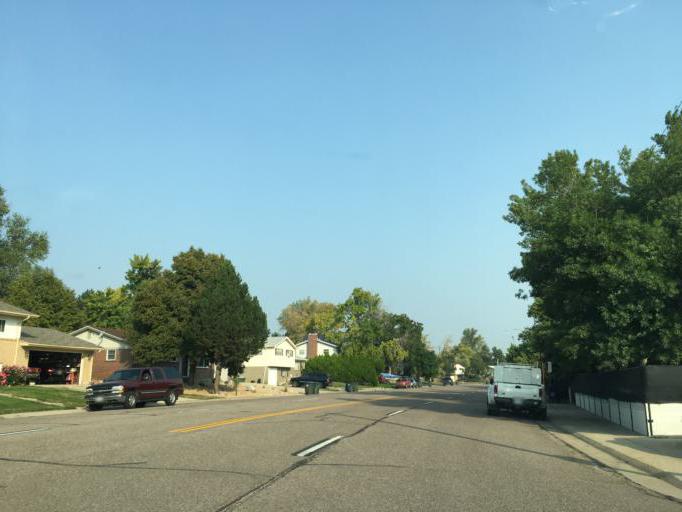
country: US
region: Colorado
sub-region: Adams County
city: Northglenn
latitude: 39.8787
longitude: -104.9899
